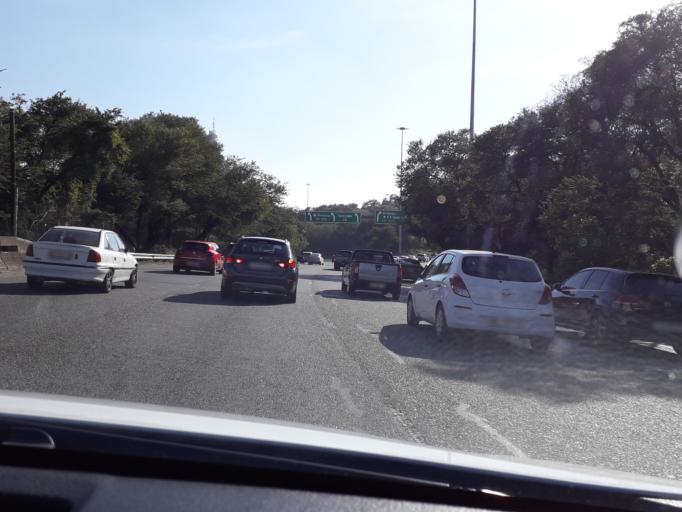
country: ZA
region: Gauteng
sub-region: City of Tshwane Metropolitan Municipality
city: Pretoria
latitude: -25.7740
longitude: 28.1952
